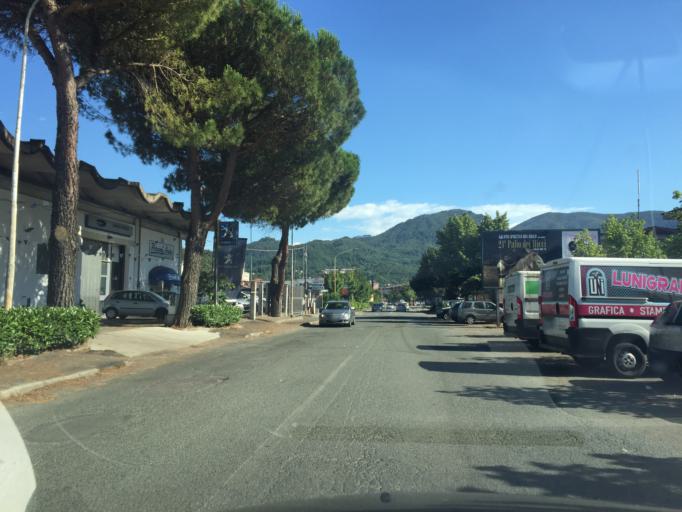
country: IT
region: Tuscany
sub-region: Provincia di Massa-Carrara
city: Terrarossa
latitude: 44.2182
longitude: 9.9661
